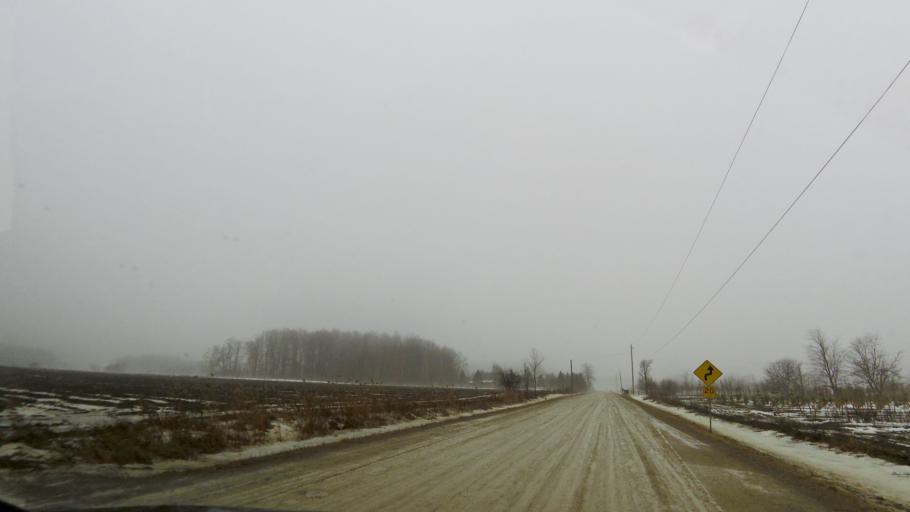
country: CA
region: Ontario
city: Brampton
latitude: 43.8482
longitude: -79.8433
